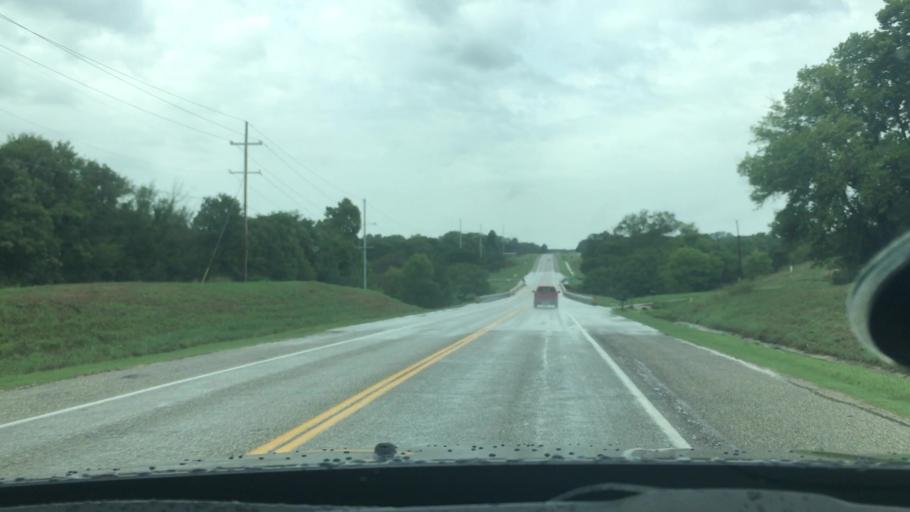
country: US
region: Oklahoma
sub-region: Johnston County
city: Tishomingo
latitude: 34.2369
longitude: -96.7152
